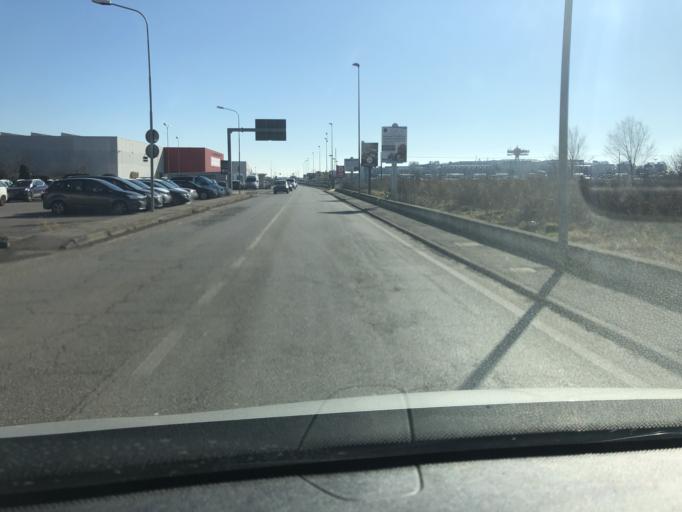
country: IT
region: Veneto
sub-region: Provincia di Verona
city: Lugagnano
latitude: 45.4441
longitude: 10.8652
